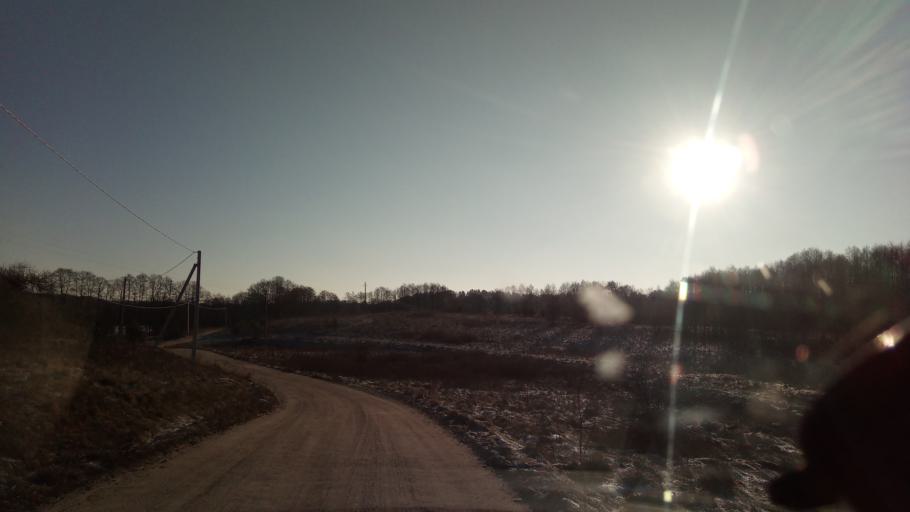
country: LT
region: Alytaus apskritis
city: Druskininkai
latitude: 54.1049
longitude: 24.0126
